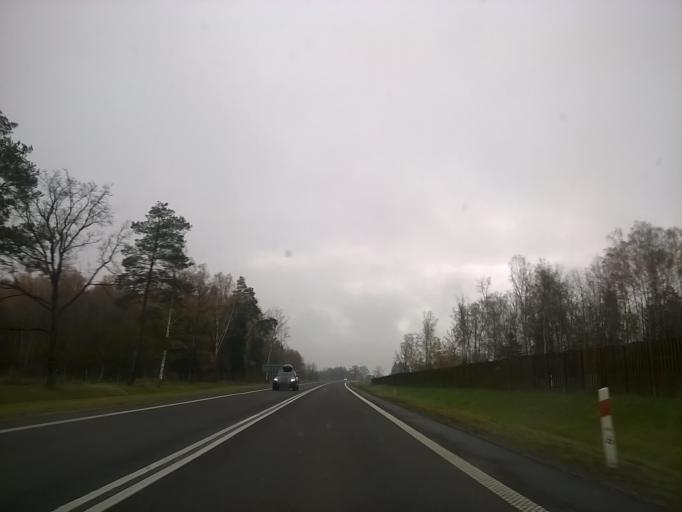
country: PL
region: Warmian-Masurian Voivodeship
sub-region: Powiat elblaski
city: Mlynary
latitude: 54.2635
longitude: 19.7211
